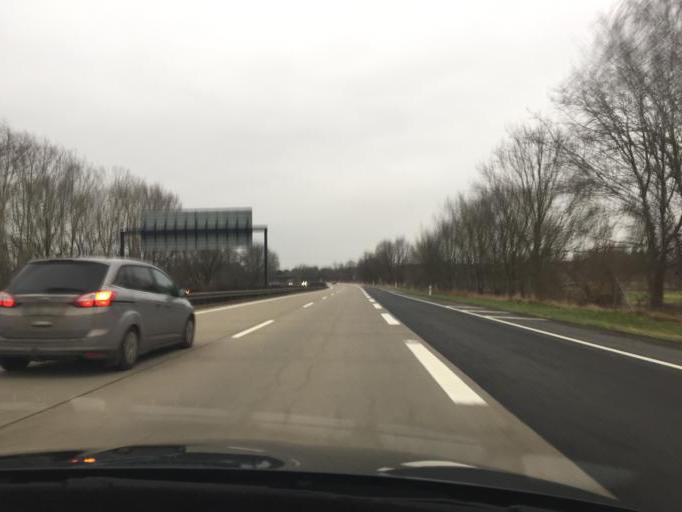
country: DE
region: Brandenburg
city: Lubbenau
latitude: 51.8421
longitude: 13.9302
